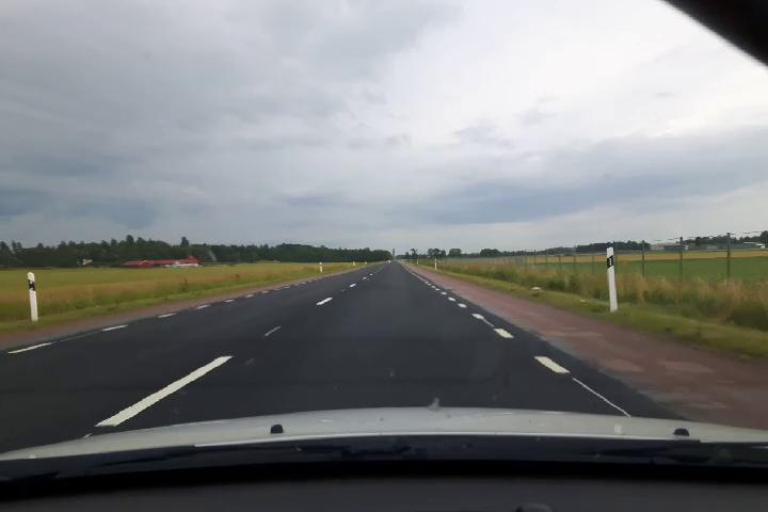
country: SE
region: Uppsala
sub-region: Uppsala Kommun
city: Gamla Uppsala
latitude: 59.8954
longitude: 17.6147
